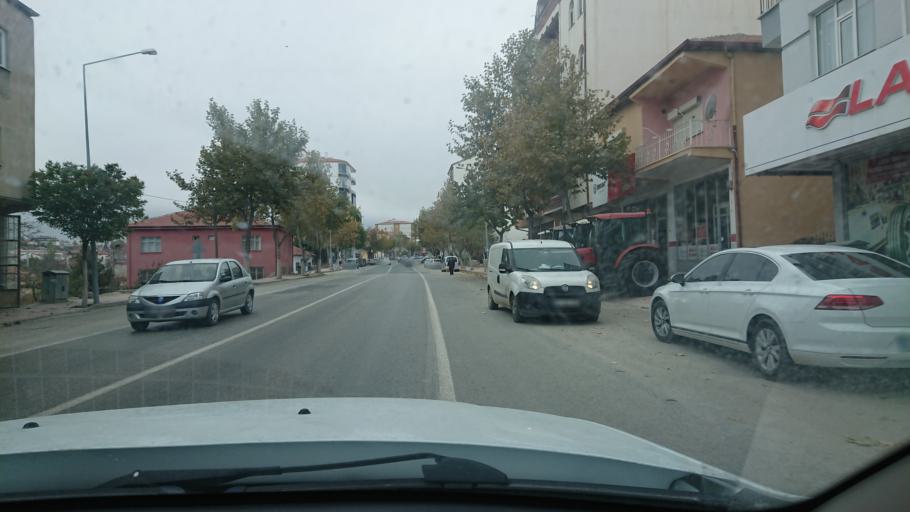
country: TR
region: Aksaray
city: Ortakoy
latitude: 38.7418
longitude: 34.0457
